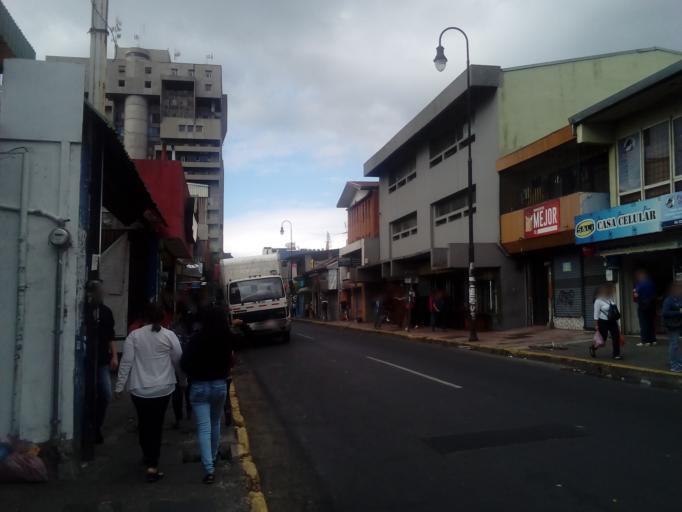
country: CR
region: San Jose
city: San Jose
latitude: 9.9306
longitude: -84.0761
